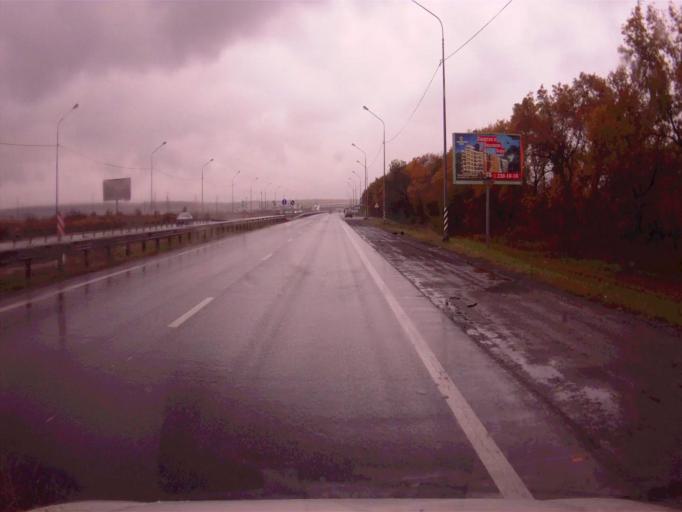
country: RU
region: Chelyabinsk
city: Dolgoderevenskoye
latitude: 55.3053
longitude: 61.3358
